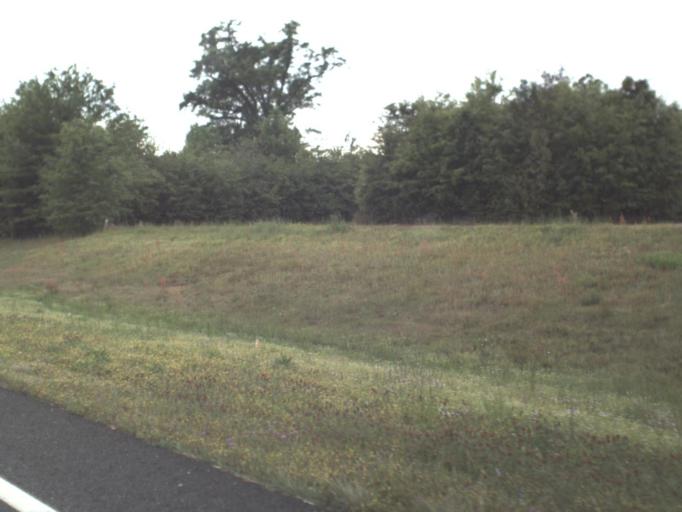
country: US
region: Florida
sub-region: Escambia County
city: Century
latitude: 30.9403
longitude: -87.2920
